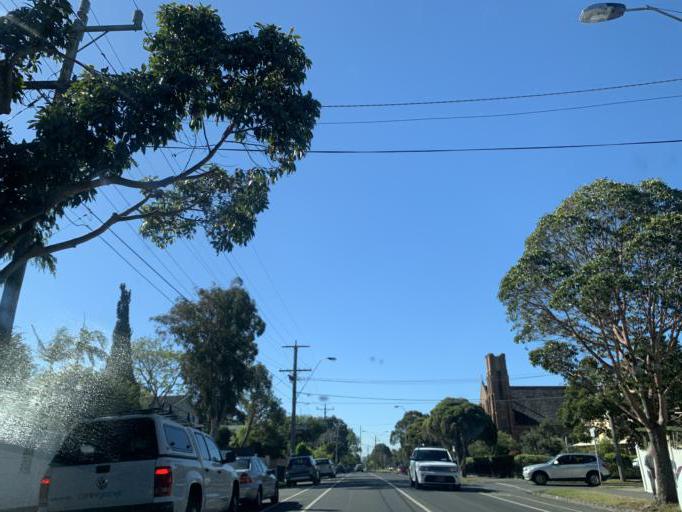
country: AU
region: Victoria
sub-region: Bayside
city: North Brighton
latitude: -37.9211
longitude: 144.9935
